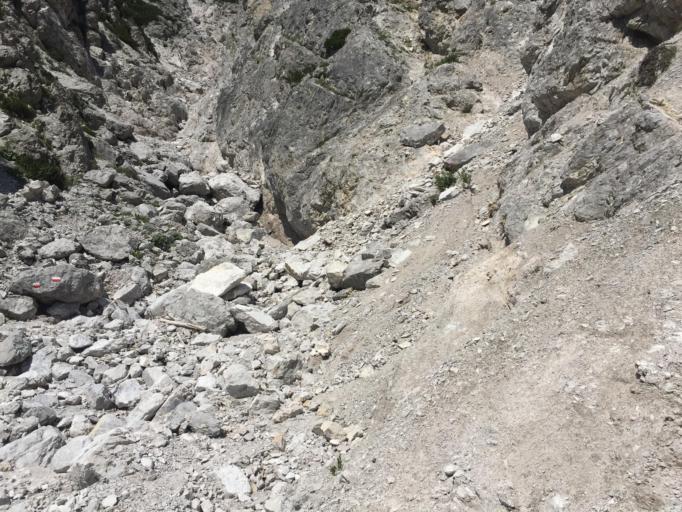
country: IT
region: Friuli Venezia Giulia
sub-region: Provincia di Udine
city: Malborghetto
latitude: 46.4660
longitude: 13.4332
